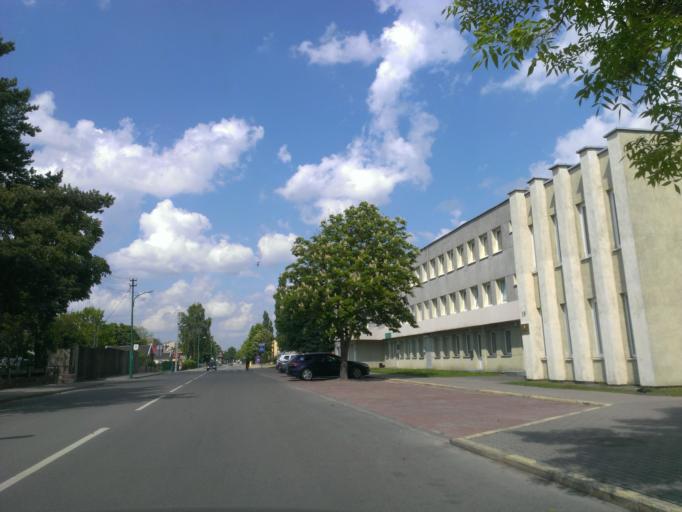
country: LT
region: Klaipedos apskritis
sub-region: Klaipeda
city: Palanga
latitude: 55.9217
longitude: 21.0736
